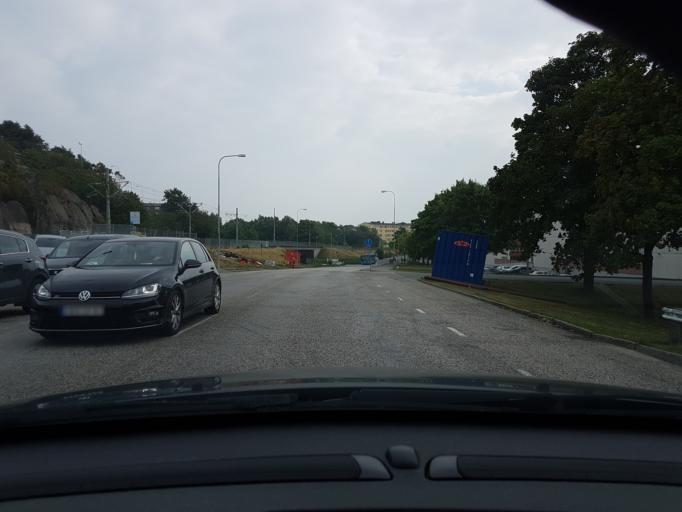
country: SE
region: Vaestra Goetaland
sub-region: Goteborg
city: Majorna
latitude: 57.6488
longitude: 11.9031
